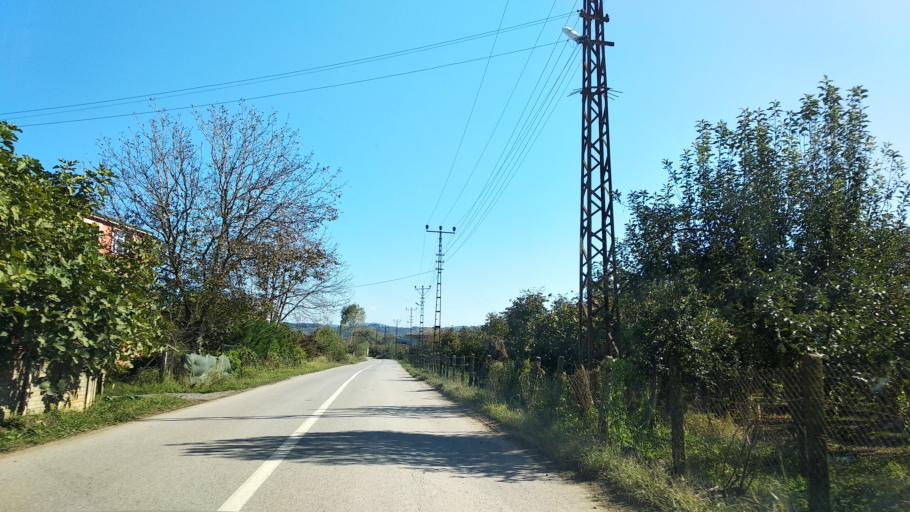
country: TR
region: Sakarya
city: Ortakoy
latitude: 41.0266
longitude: 30.5971
